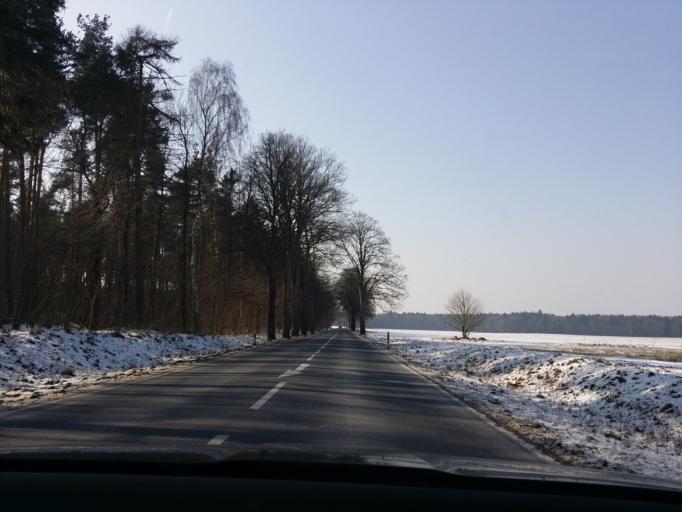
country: DE
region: Brandenburg
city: Heiligengrabe
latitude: 53.1392
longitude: 12.3215
